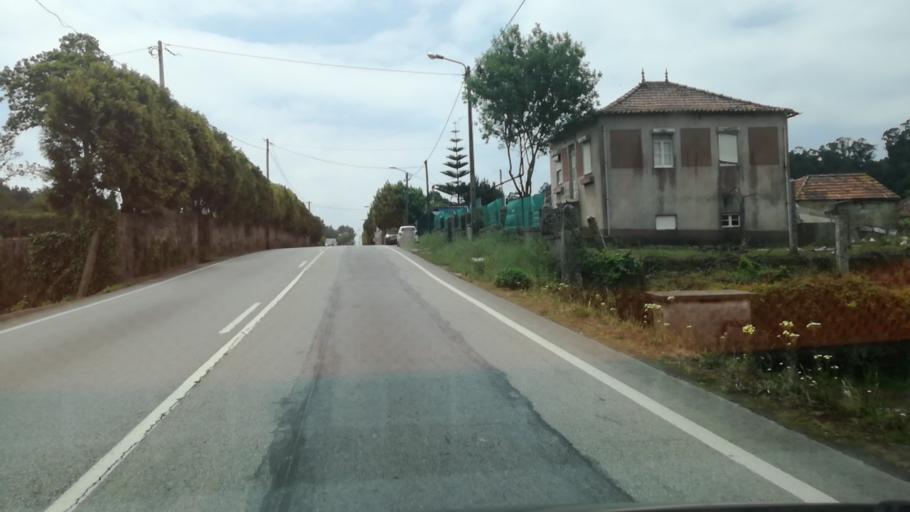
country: PT
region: Porto
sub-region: Trofa
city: Sao Romao do Coronado
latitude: 41.2933
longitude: -8.6006
